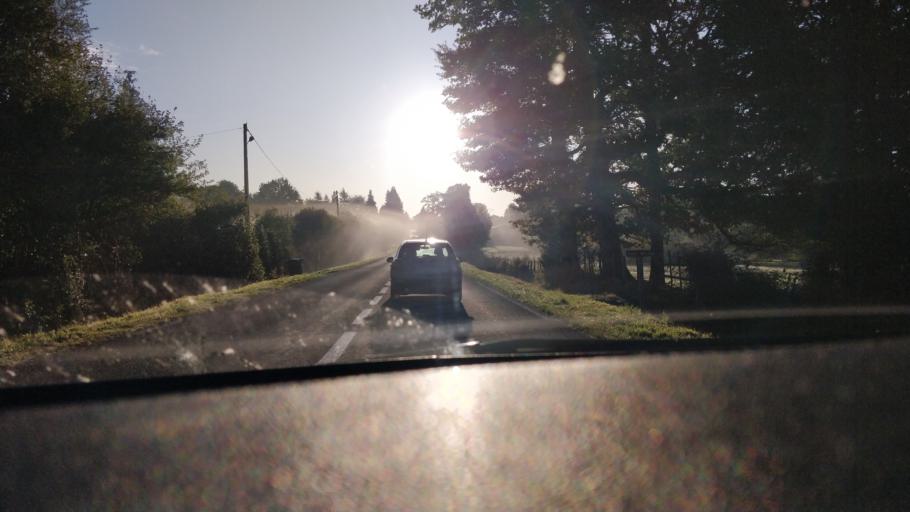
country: FR
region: Limousin
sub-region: Departement de la Creuse
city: Bourganeuf
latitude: 45.9484
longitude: 1.6958
